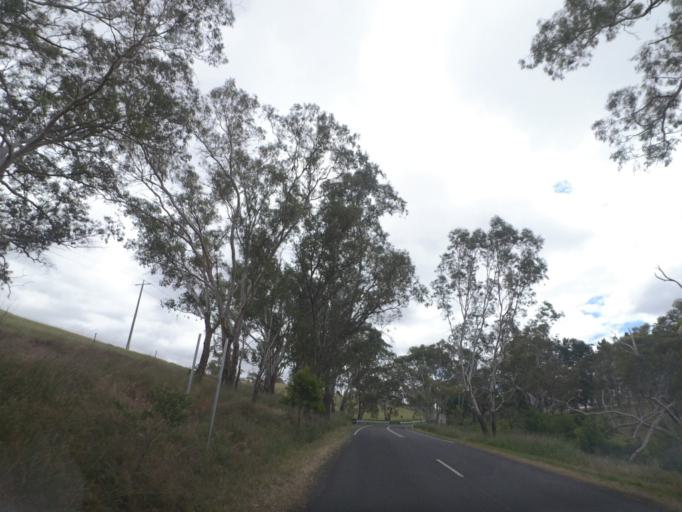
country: AU
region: Victoria
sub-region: Whittlesea
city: Whittlesea
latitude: -37.1916
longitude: 145.0385
